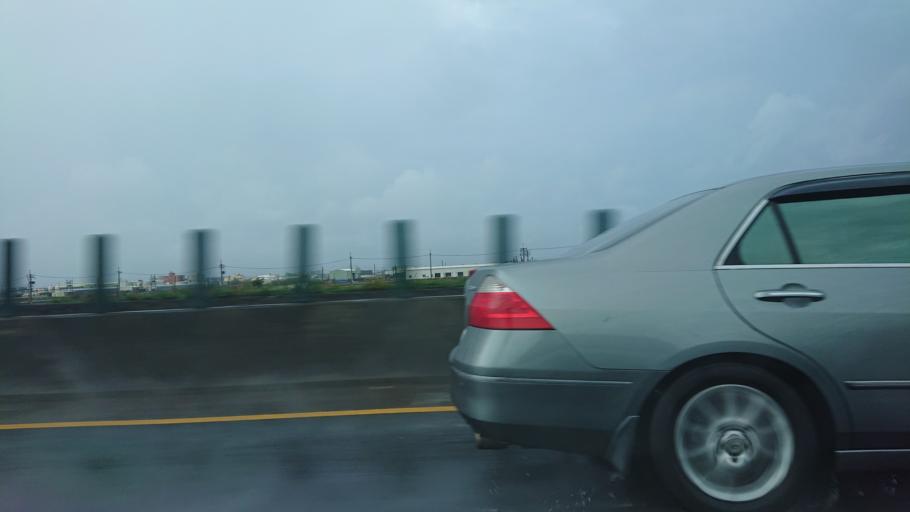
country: TW
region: Taiwan
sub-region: Changhua
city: Chang-hua
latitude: 24.1300
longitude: 120.4394
